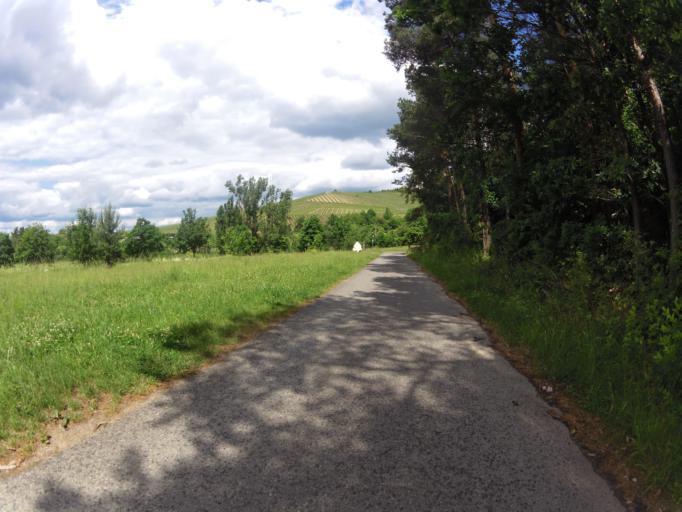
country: DE
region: Bavaria
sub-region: Regierungsbezirk Unterfranken
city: Thungersheim
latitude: 49.8773
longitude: 9.8590
